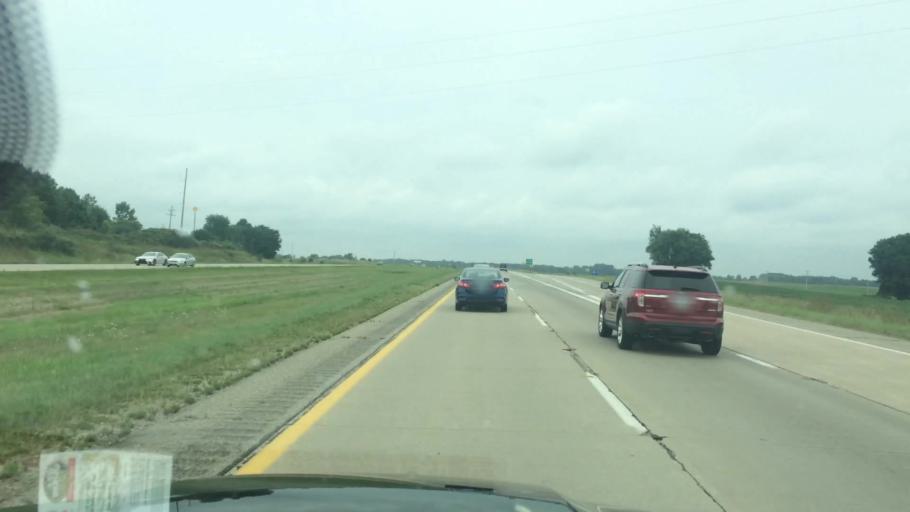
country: US
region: Michigan
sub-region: Eaton County
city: Potterville
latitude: 42.6178
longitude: -84.7444
